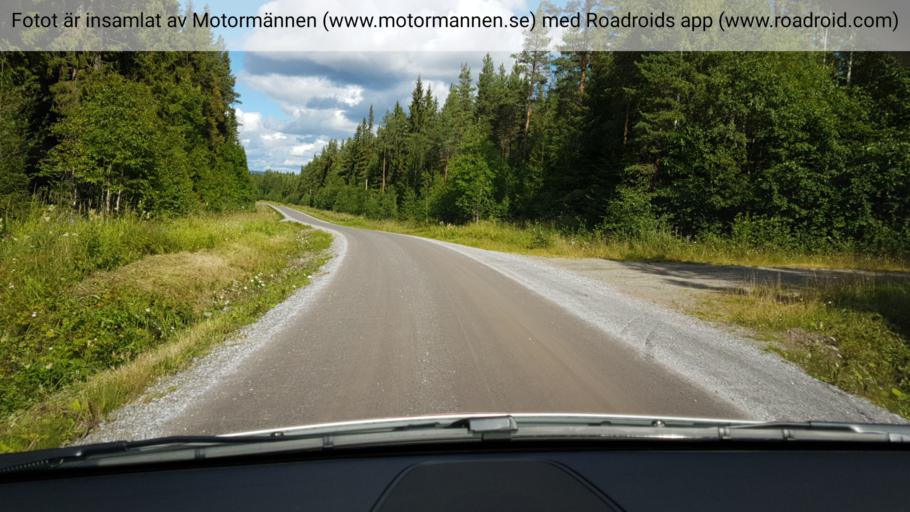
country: SE
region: Jaemtland
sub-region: Braecke Kommun
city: Braecke
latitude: 63.1299
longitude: 15.7589
